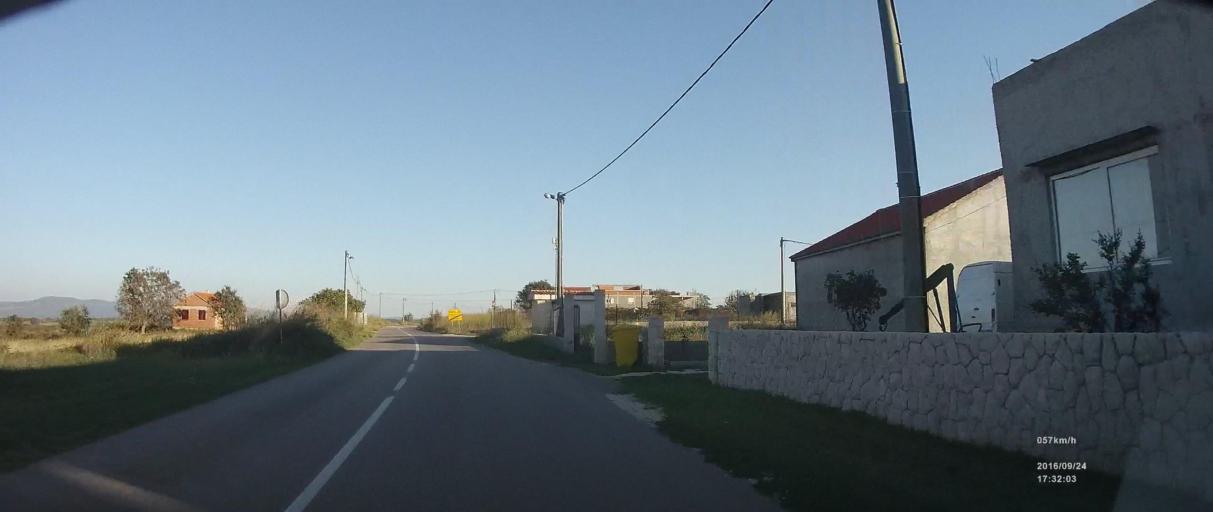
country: HR
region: Zadarska
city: Posedarje
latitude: 44.1847
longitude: 15.4471
